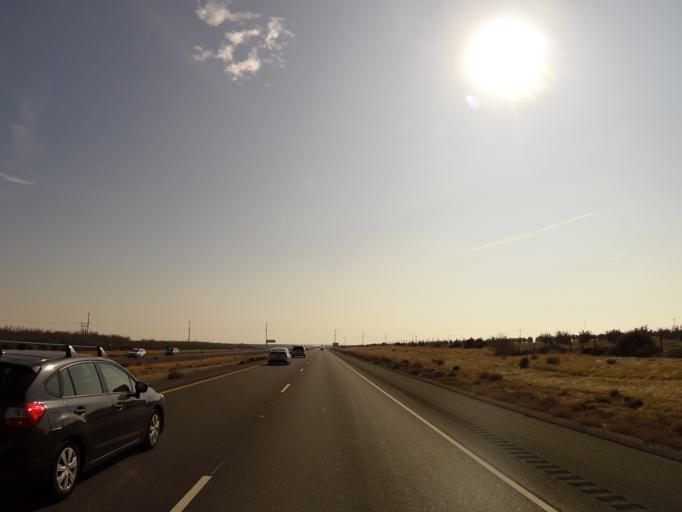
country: US
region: California
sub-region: Kings County
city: Kettleman City
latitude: 35.9502
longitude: -119.9284
